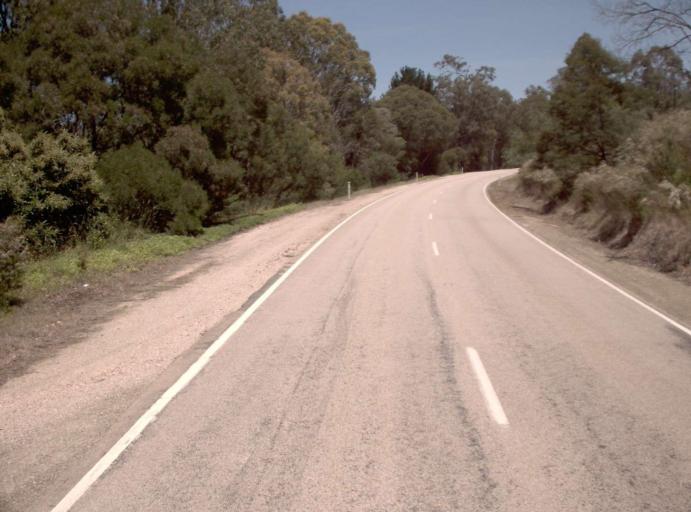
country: AU
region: Victoria
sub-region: East Gippsland
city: Lakes Entrance
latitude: -37.6703
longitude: 147.8685
